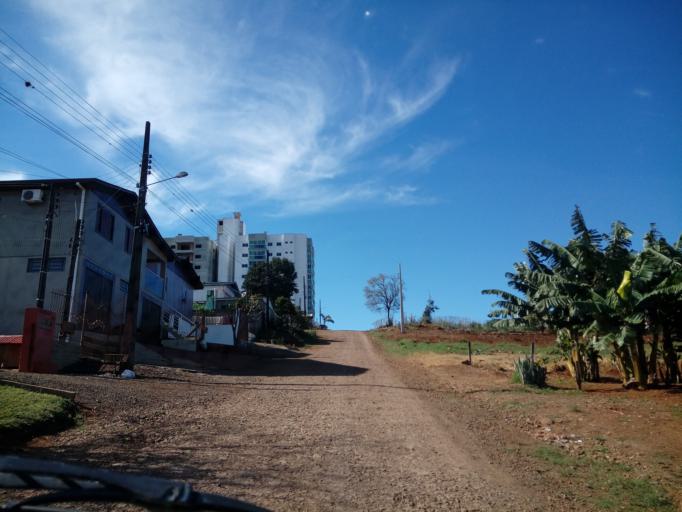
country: BR
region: Santa Catarina
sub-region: Chapeco
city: Chapeco
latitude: -27.0725
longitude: -52.6144
